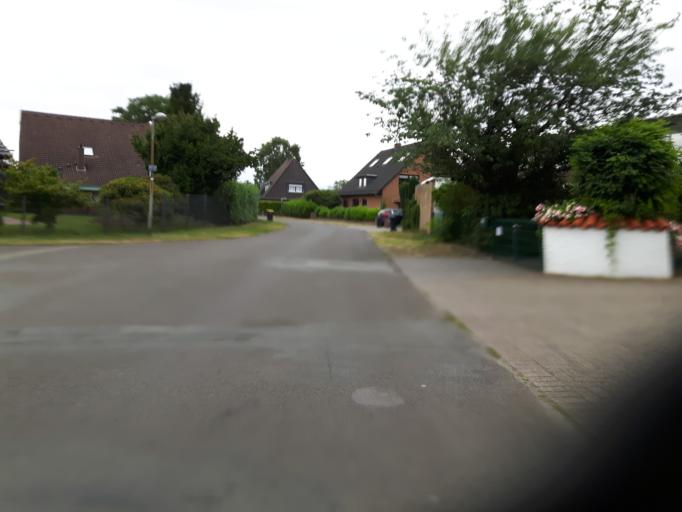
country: DE
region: Lower Saxony
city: Stuhr
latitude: 53.0295
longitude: 8.7342
